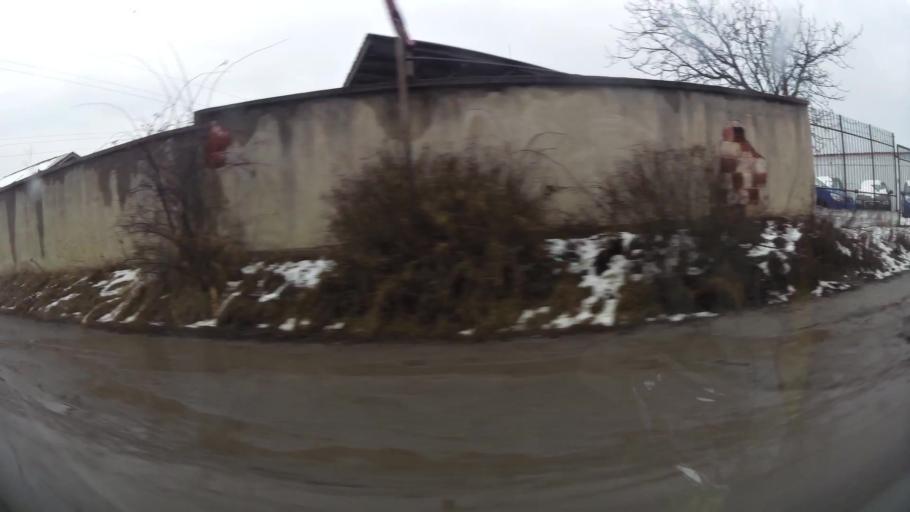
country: BG
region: Sofiya
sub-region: Obshtina Bozhurishte
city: Bozhurishte
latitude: 42.6879
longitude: 23.2317
